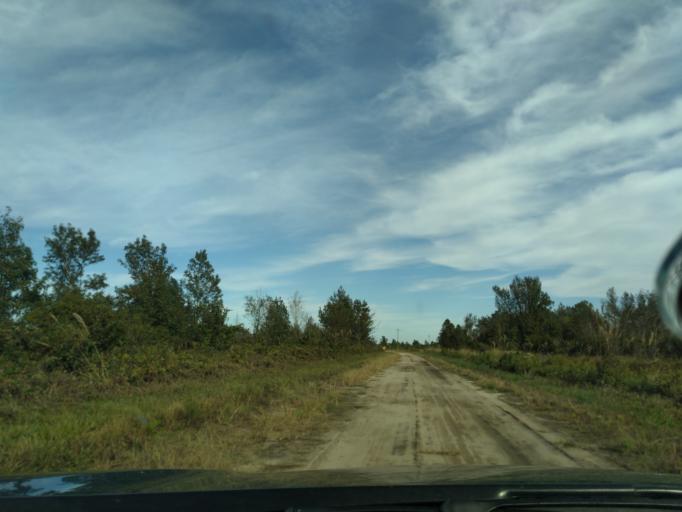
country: US
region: North Carolina
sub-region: Beaufort County
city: Belhaven
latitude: 35.6901
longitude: -76.5450
